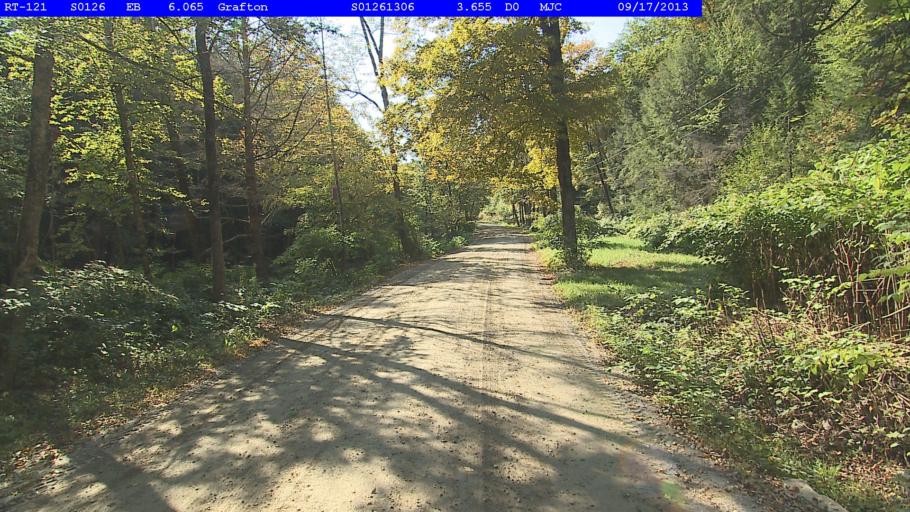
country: US
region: Vermont
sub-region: Windsor County
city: Chester
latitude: 43.1964
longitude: -72.6192
